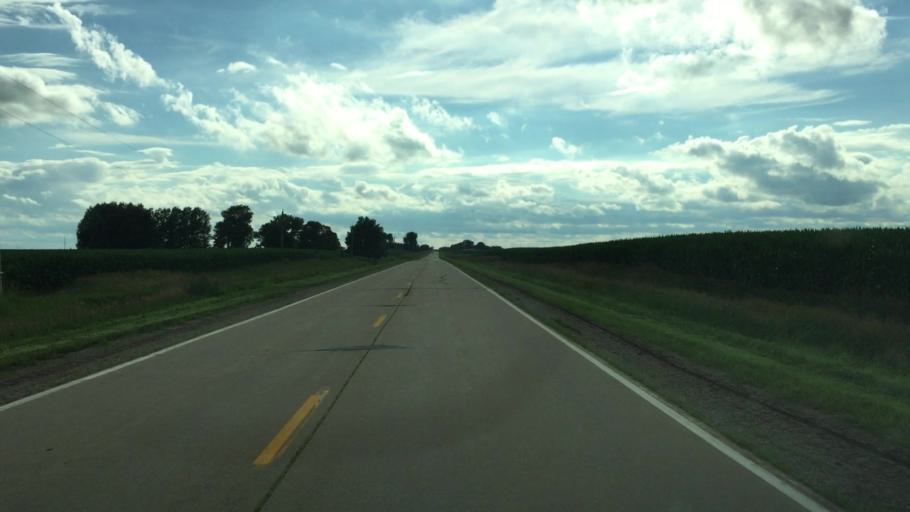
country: US
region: Iowa
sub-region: Jasper County
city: Prairie City
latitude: 41.5806
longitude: -93.1642
